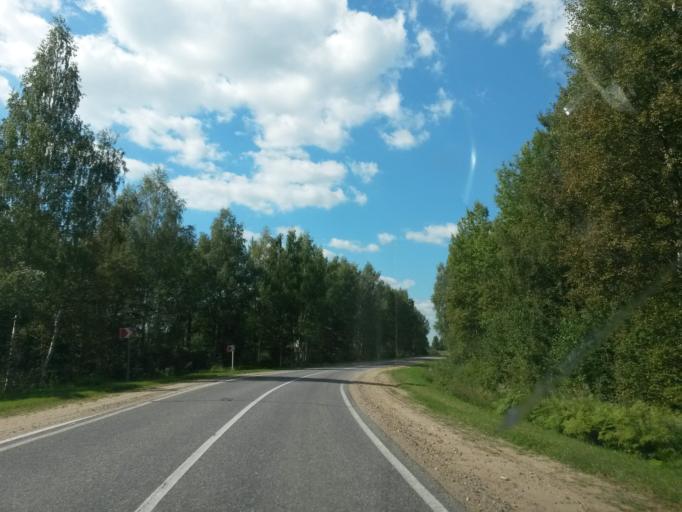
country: RU
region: Jaroslavl
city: Tunoshna
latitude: 57.4729
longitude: 40.1710
